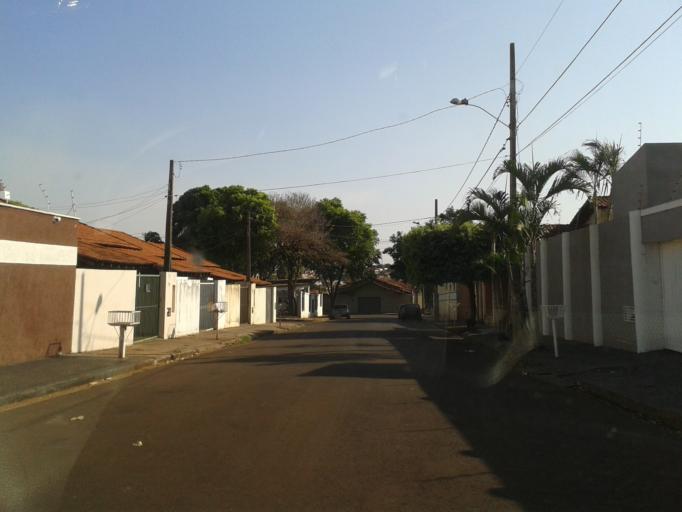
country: BR
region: Minas Gerais
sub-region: Ituiutaba
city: Ituiutaba
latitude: -18.9700
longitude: -49.4495
